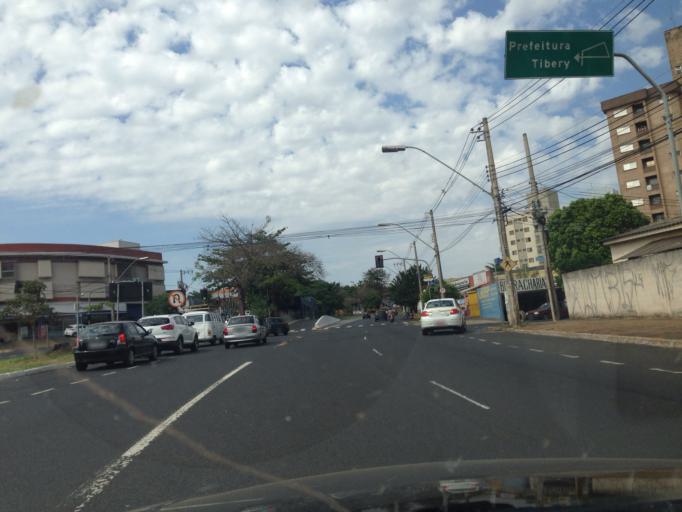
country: BR
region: Minas Gerais
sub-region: Uberlandia
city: Uberlandia
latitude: -18.9135
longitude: -48.2589
